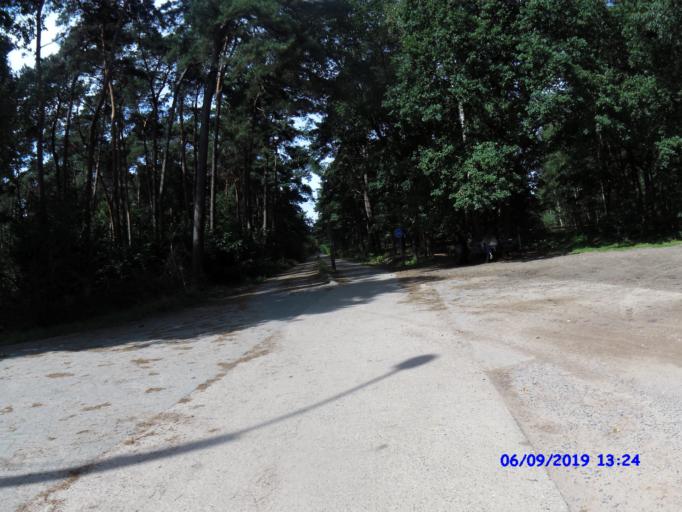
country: BE
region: Flanders
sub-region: Provincie Antwerpen
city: Kasterlee
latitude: 51.2192
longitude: 5.0022
